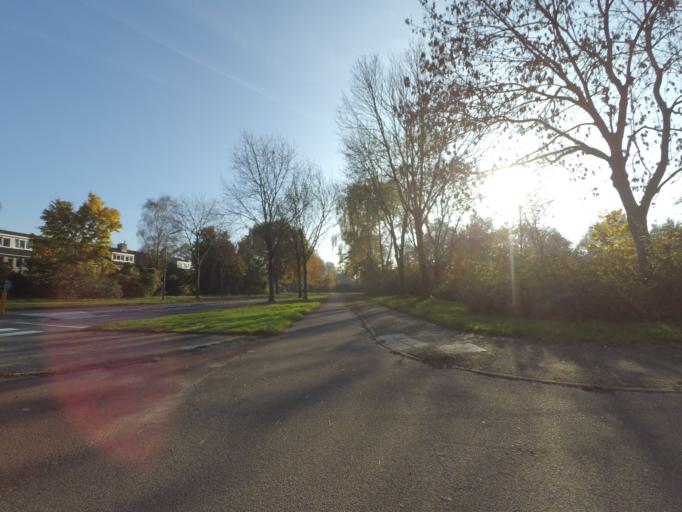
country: NL
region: Utrecht
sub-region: Gemeente Leusden
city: Leusden
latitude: 52.1322
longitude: 5.4226
